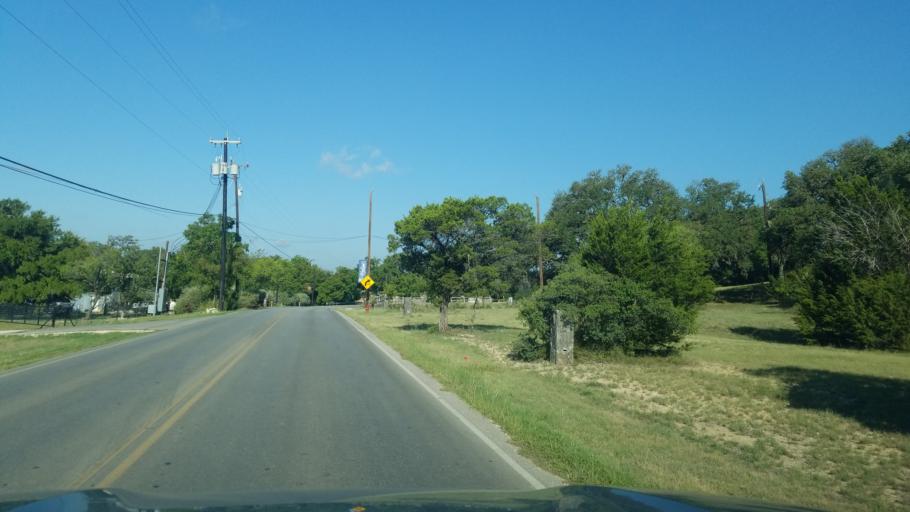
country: US
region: Texas
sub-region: Comal County
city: Bulverde
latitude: 29.7428
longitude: -98.4484
